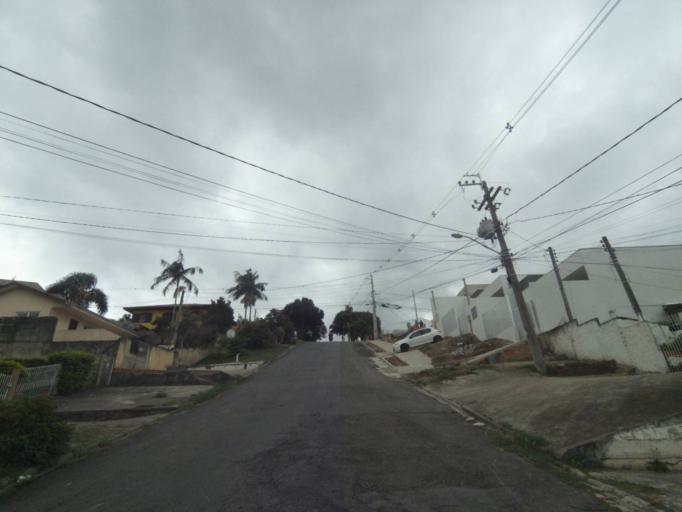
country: BR
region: Parana
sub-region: Curitiba
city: Curitiba
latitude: -25.4778
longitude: -49.2728
